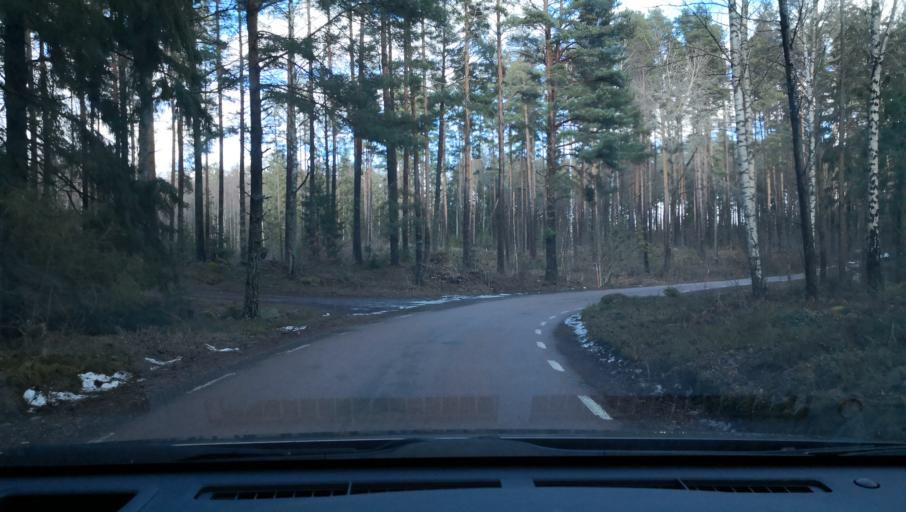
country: SE
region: Vaestmanland
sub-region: Arboga Kommun
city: Arboga
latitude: 59.3198
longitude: 15.7749
